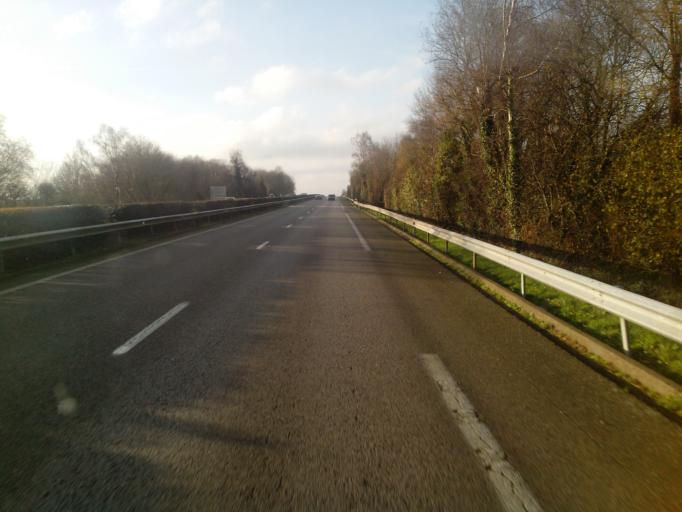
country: FR
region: Brittany
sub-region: Departement du Morbihan
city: Taupont
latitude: 47.9362
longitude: -2.4422
